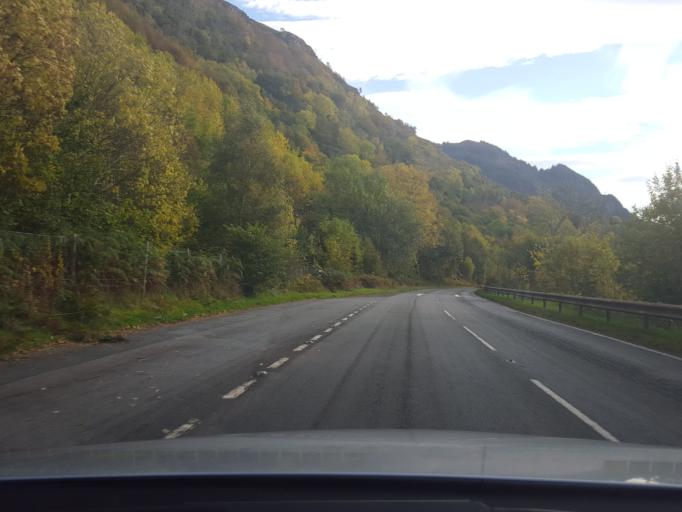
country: GB
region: Scotland
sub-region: Highland
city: Fort William
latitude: 57.2573
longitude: -5.4838
